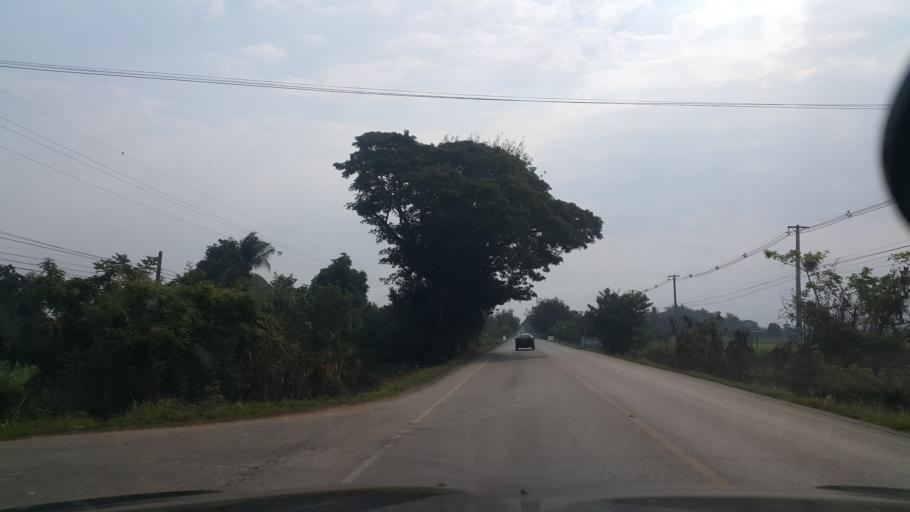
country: TH
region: Sukhothai
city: Si Samrong
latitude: 17.1813
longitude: 99.8362
